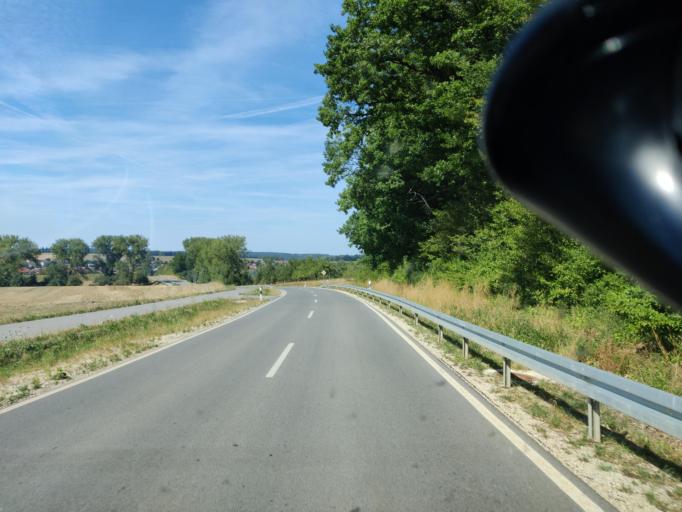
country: DE
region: Bavaria
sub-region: Regierungsbezirk Mittelfranken
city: Thalmassing
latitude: 49.1210
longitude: 11.2133
